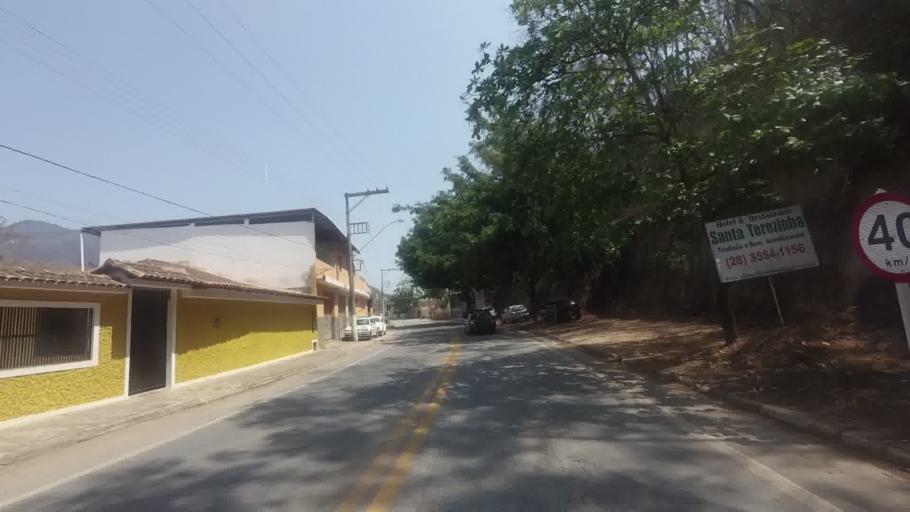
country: BR
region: Espirito Santo
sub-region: Mimoso Do Sul
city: Mimoso do Sul
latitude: -20.9440
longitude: -41.3351
